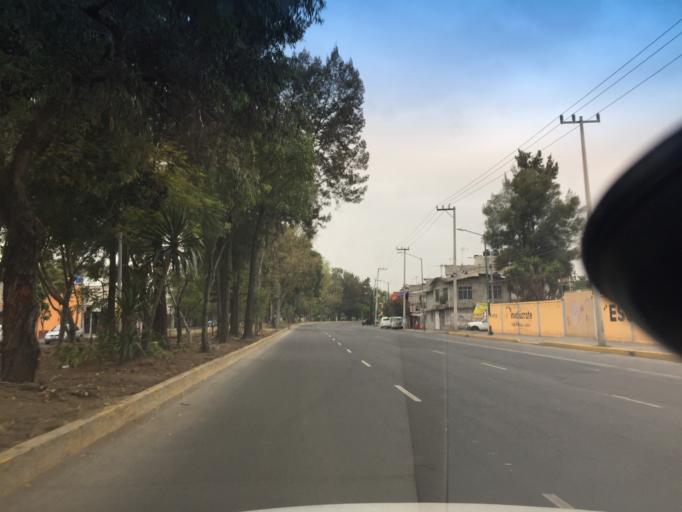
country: MX
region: Mexico City
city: Venustiano Carranza
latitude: 19.4670
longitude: -99.0765
